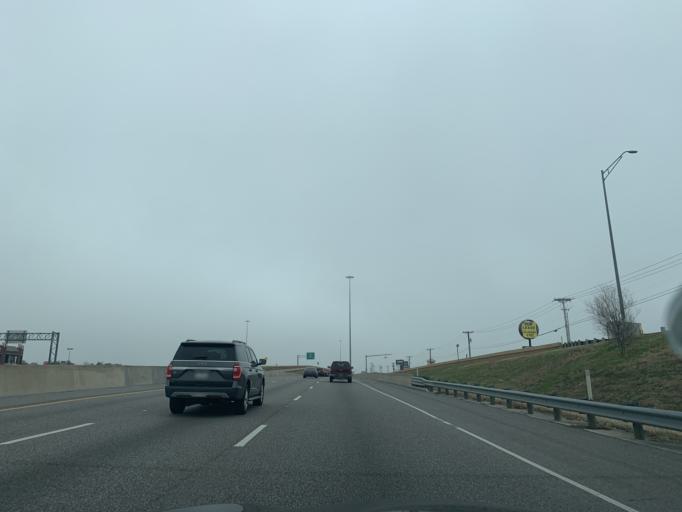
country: US
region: Texas
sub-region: Tarrant County
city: Bedford
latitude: 32.8374
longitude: -97.1180
